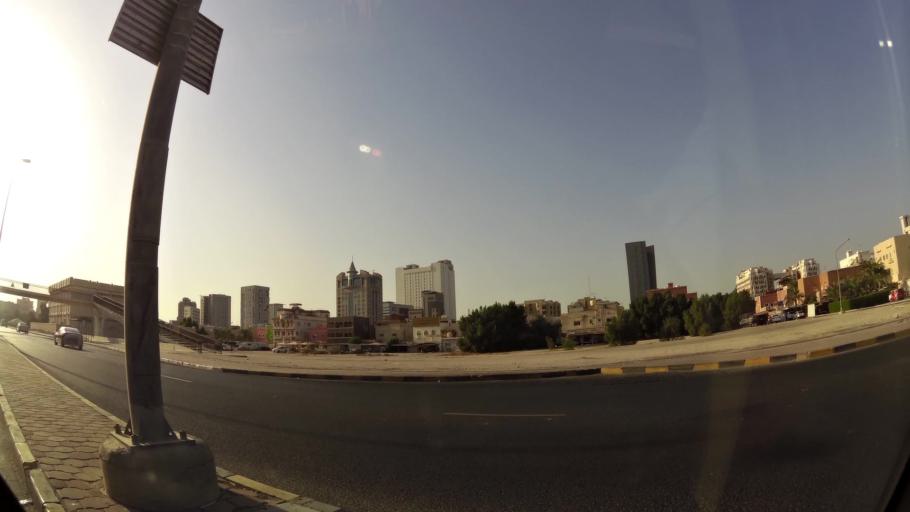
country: KW
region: Muhafazat Hawalli
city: As Salimiyah
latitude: 29.3399
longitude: 48.0810
